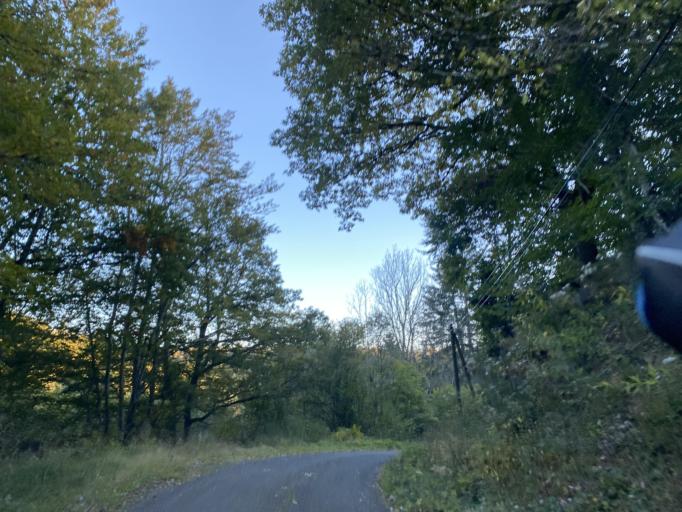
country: FR
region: Rhone-Alpes
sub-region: Departement de la Loire
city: Saint-Just-en-Chevalet
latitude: 45.9547
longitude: 3.8625
